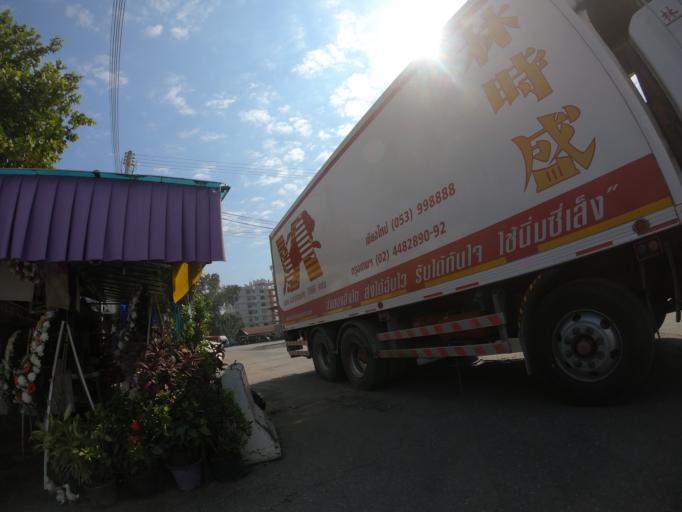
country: TH
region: Chiang Mai
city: Chiang Mai
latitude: 18.8089
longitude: 99.0090
